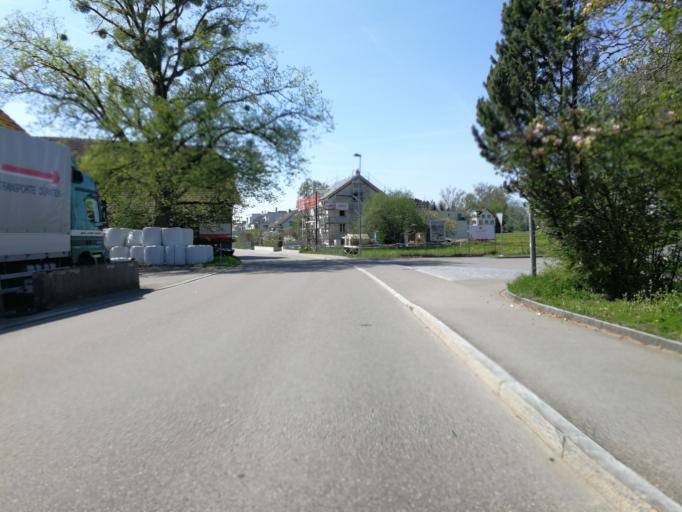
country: CH
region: Zurich
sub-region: Bezirk Hinwil
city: Durnten
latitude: 47.2778
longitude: 8.8384
